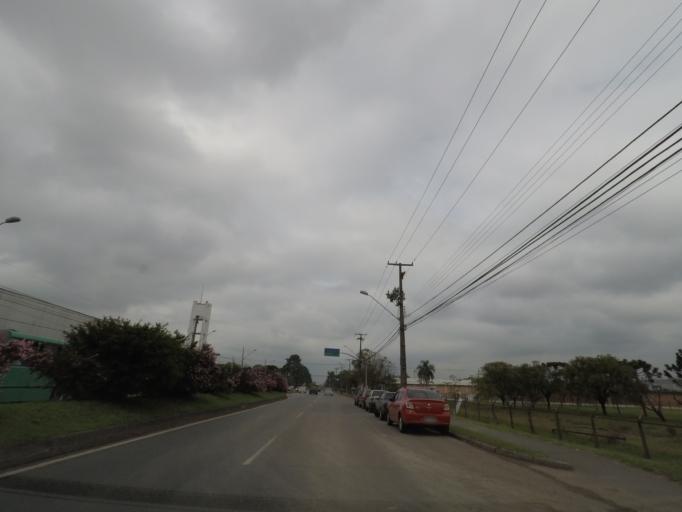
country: BR
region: Parana
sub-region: Curitiba
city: Curitiba
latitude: -25.5007
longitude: -49.3271
